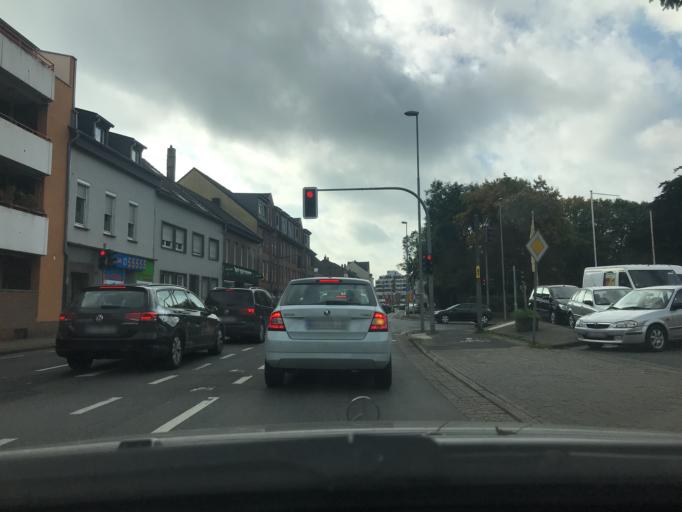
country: DE
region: North Rhine-Westphalia
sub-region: Regierungsbezirk Dusseldorf
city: Moers
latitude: 51.4560
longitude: 6.6292
